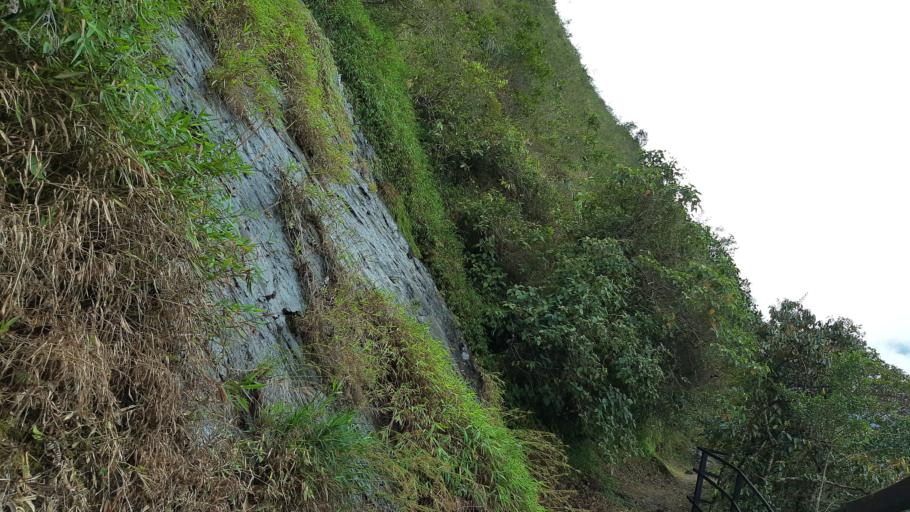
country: CO
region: Boyaca
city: Santa Maria
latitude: 4.9156
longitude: -73.3023
